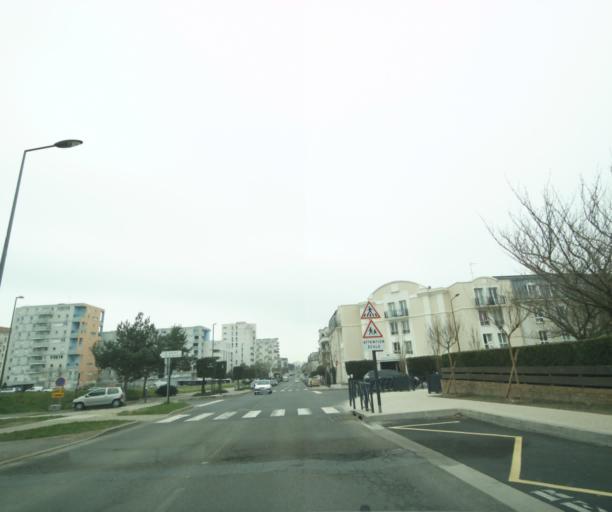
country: FR
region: Ile-de-France
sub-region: Departement du Val-d'Oise
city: Courdimanche
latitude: 49.0452
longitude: 2.0111
